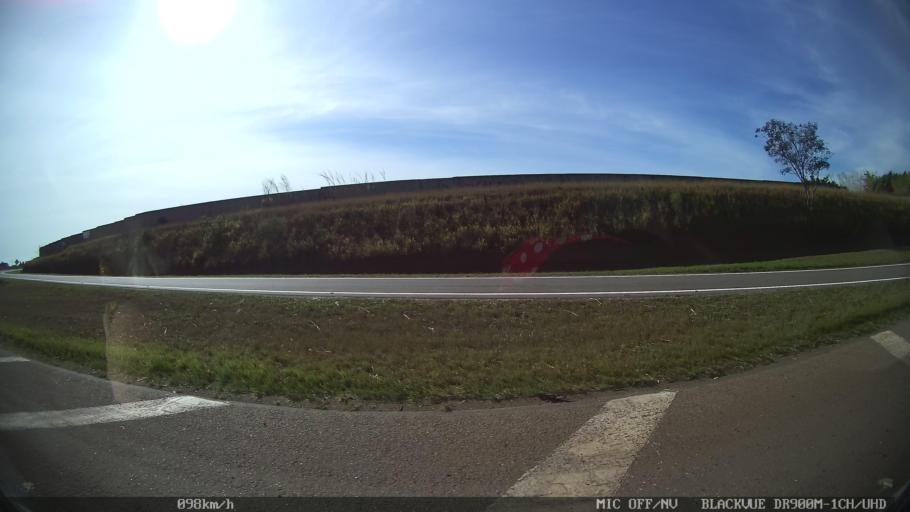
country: BR
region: Sao Paulo
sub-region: Piracicaba
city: Piracicaba
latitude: -22.7675
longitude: -47.5947
